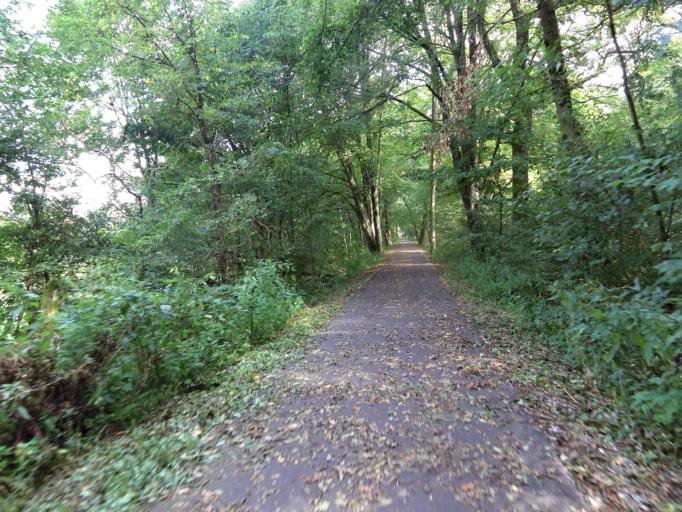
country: DE
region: Saxony-Anhalt
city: Dessau
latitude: 51.8633
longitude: 12.2884
